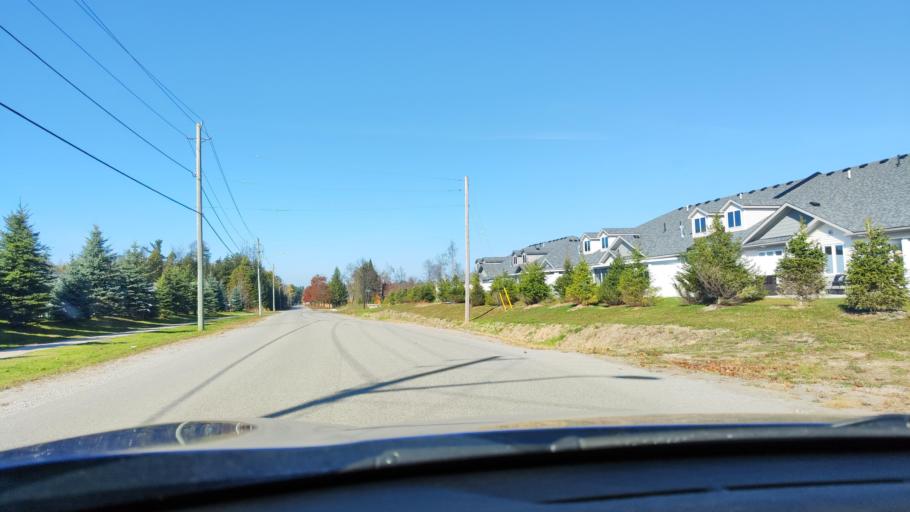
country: CA
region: Ontario
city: Wasaga Beach
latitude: 44.5291
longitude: -79.9974
